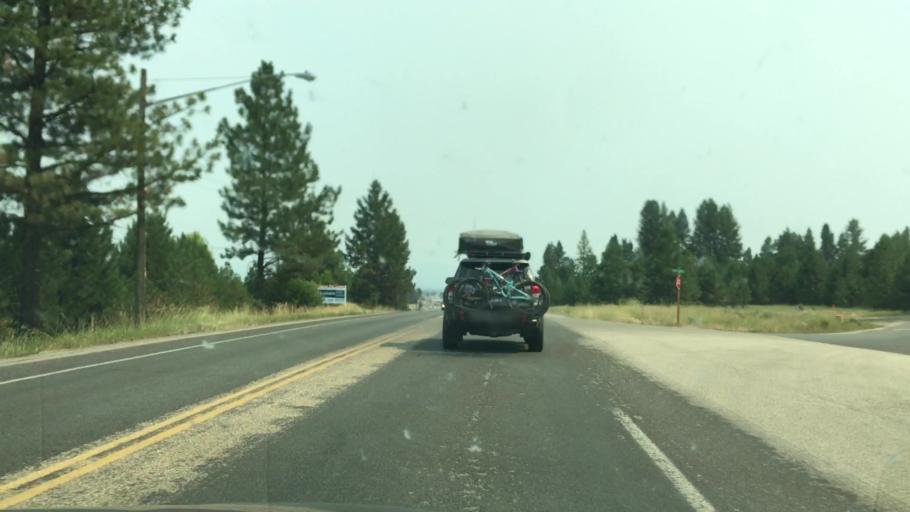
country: US
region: Idaho
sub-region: Valley County
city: Cascade
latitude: 44.5095
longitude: -116.0352
